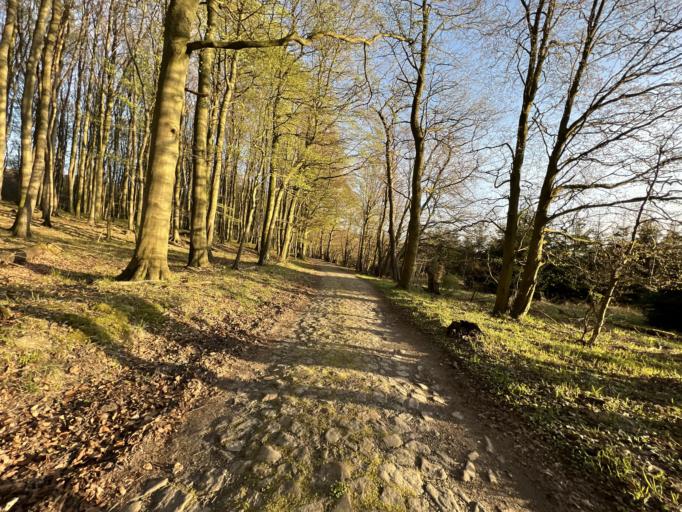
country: DE
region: Mecklenburg-Vorpommern
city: Sassnitz
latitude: 54.5354
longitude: 13.6533
